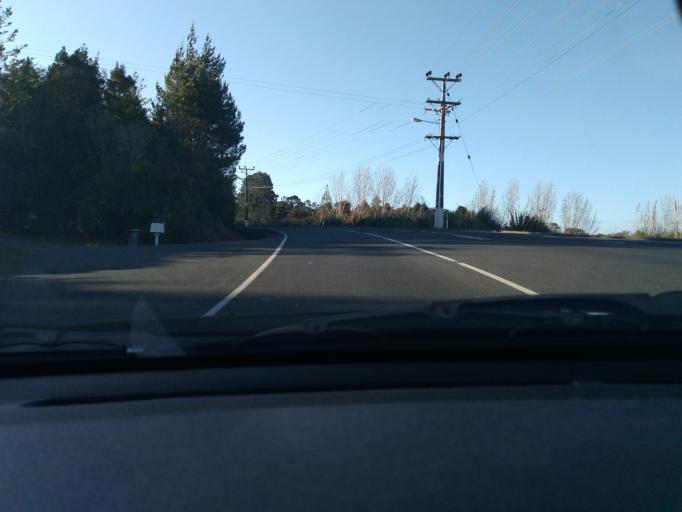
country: NZ
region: Auckland
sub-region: Auckland
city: Warkworth
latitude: -36.4075
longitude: 174.7192
